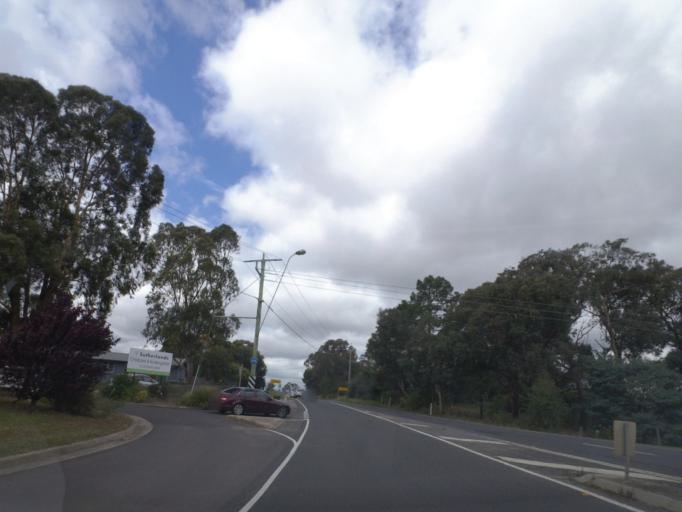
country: AU
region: Victoria
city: Plenty
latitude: -37.6776
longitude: 145.1273
